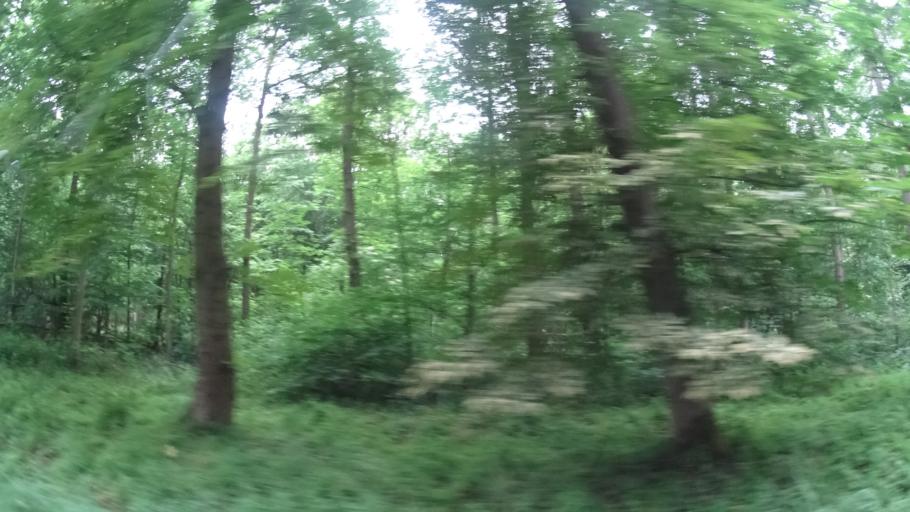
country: DE
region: Lower Saxony
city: Springe
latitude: 52.1826
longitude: 9.5904
